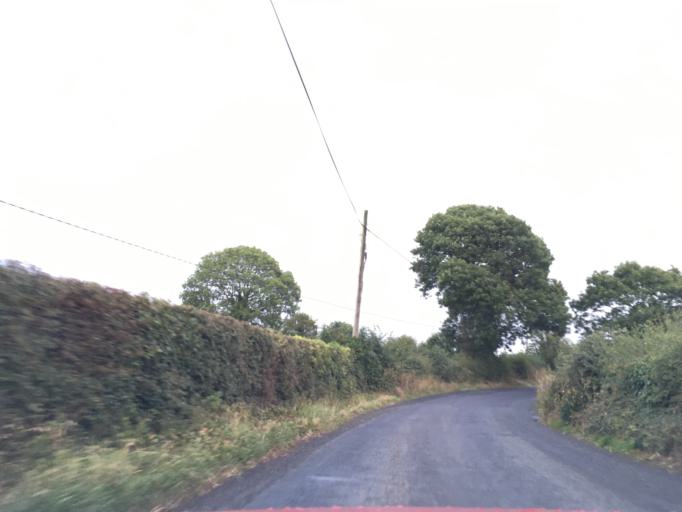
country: IE
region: Munster
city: Cahir
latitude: 52.4636
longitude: -7.9737
